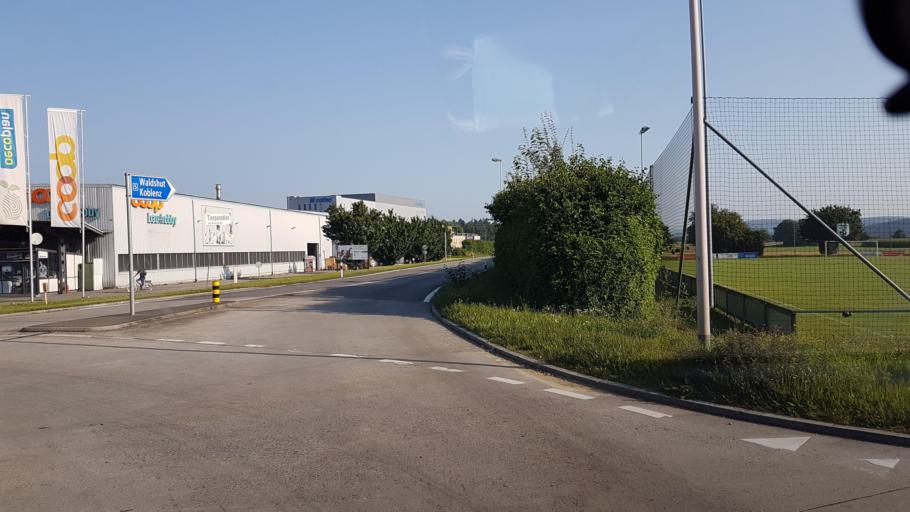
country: CH
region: Aargau
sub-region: Bezirk Baden
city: Wurenlingen
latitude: 47.5258
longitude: 8.2437
